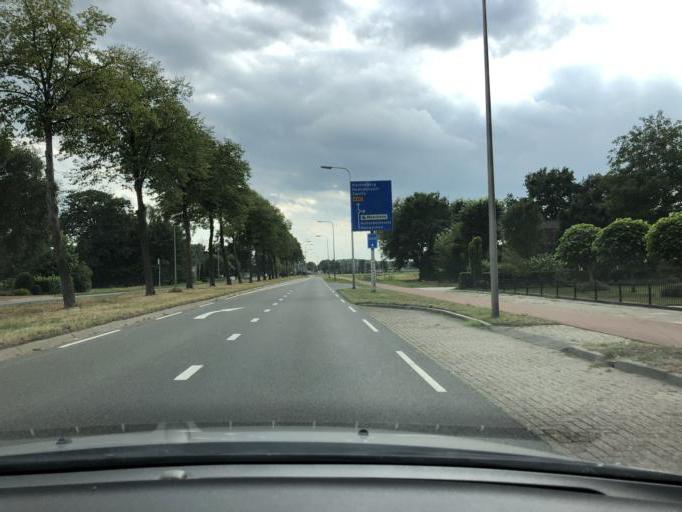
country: NL
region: Overijssel
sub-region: Gemeente Hardenberg
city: Hardenberg
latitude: 52.6230
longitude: 6.5537
